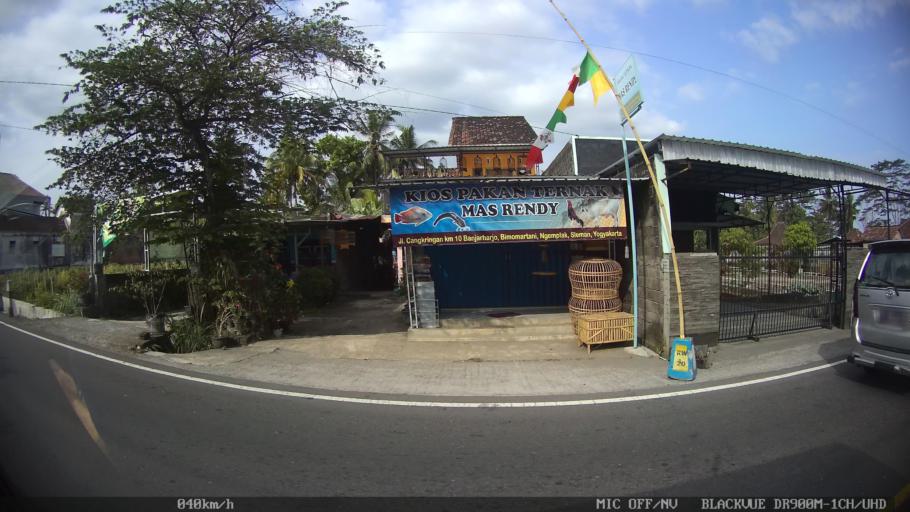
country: ID
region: Central Java
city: Candi Prambanan
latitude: -7.6839
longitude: 110.4603
